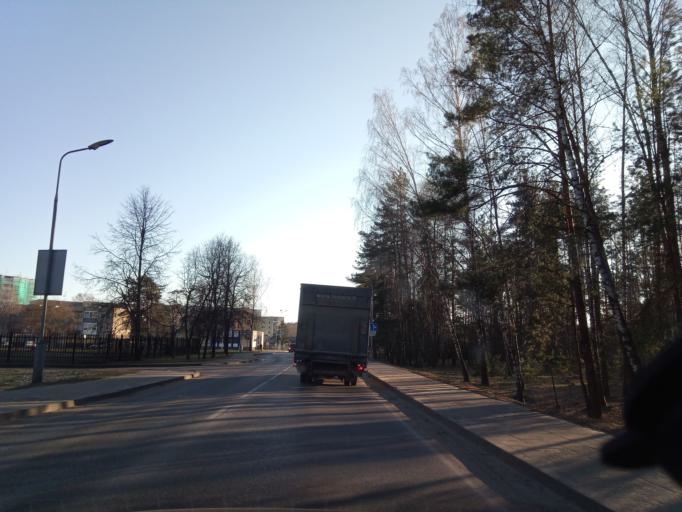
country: LT
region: Alytaus apskritis
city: Druskininkai
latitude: 54.0239
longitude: 24.0008
